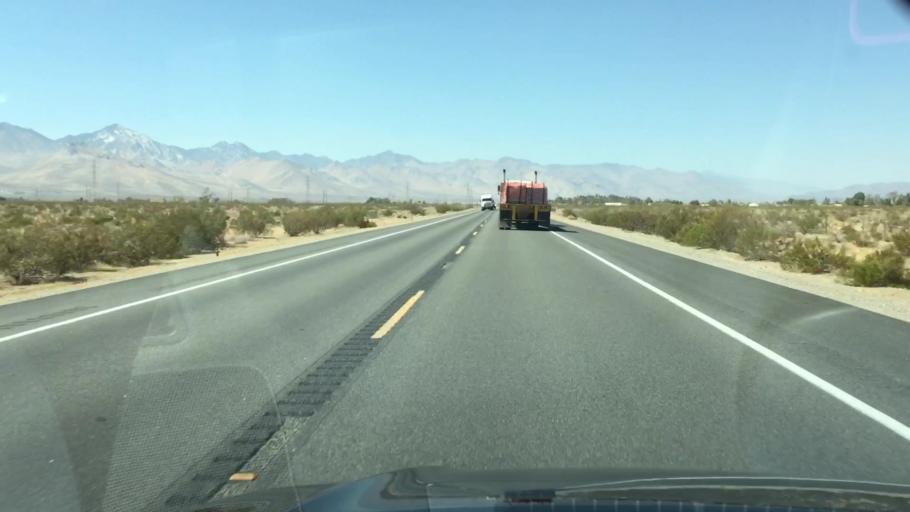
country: US
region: California
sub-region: Kern County
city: China Lake Acres
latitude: 35.6274
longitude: -117.7798
